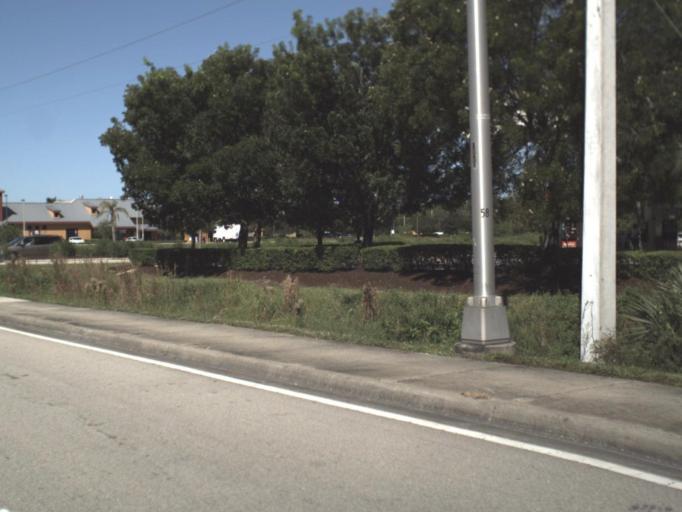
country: US
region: Florida
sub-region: Collier County
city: Vineyards
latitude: 26.2117
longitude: -81.7429
